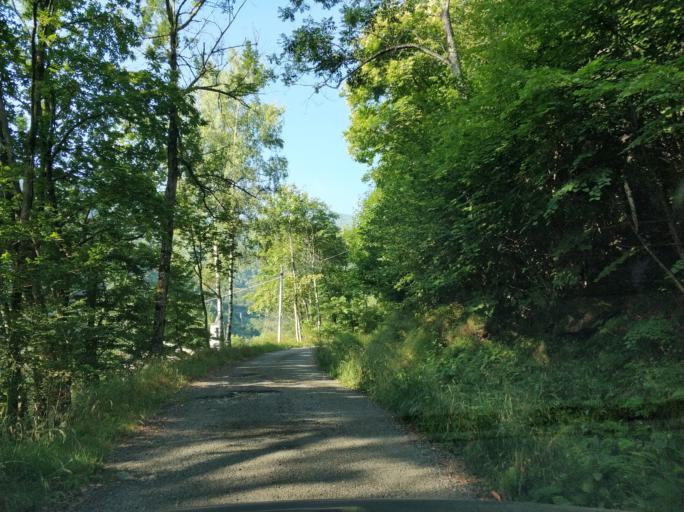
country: IT
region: Piedmont
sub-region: Provincia di Torino
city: Ceres
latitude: 45.3108
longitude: 7.3682
